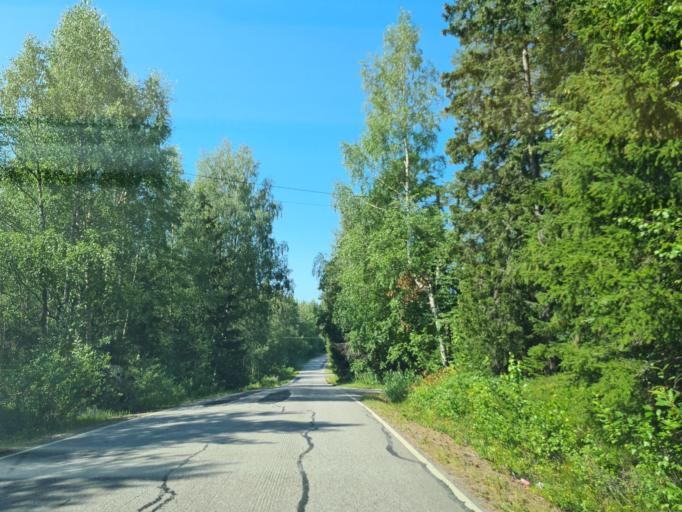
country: FI
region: Varsinais-Suomi
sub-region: Turku
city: Tarvasjoki
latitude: 60.5988
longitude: 22.6568
